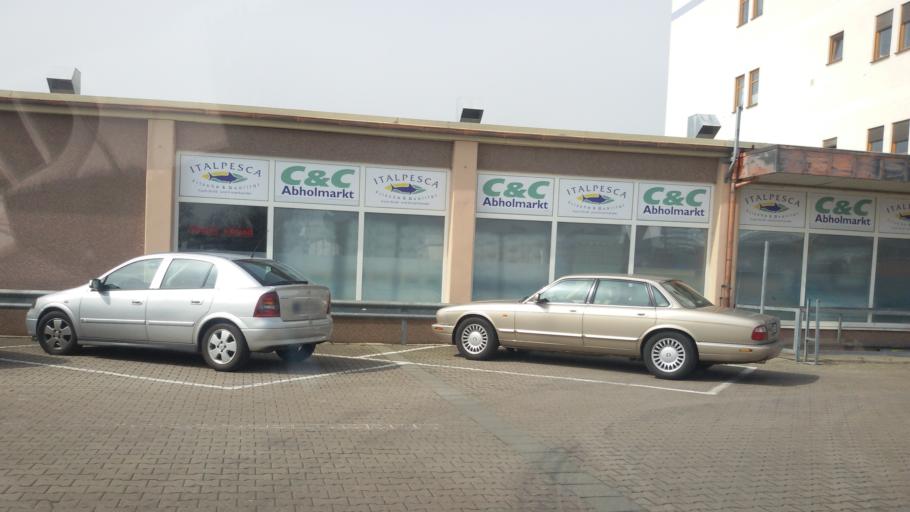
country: DE
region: Rheinland-Pfalz
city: Maxdorf
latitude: 49.4849
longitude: 8.2905
